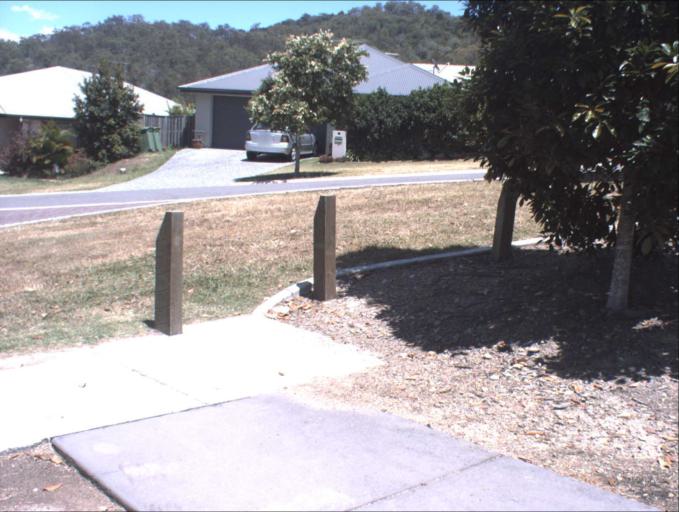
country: AU
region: Queensland
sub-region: Logan
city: Windaroo
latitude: -27.7489
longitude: 153.1851
